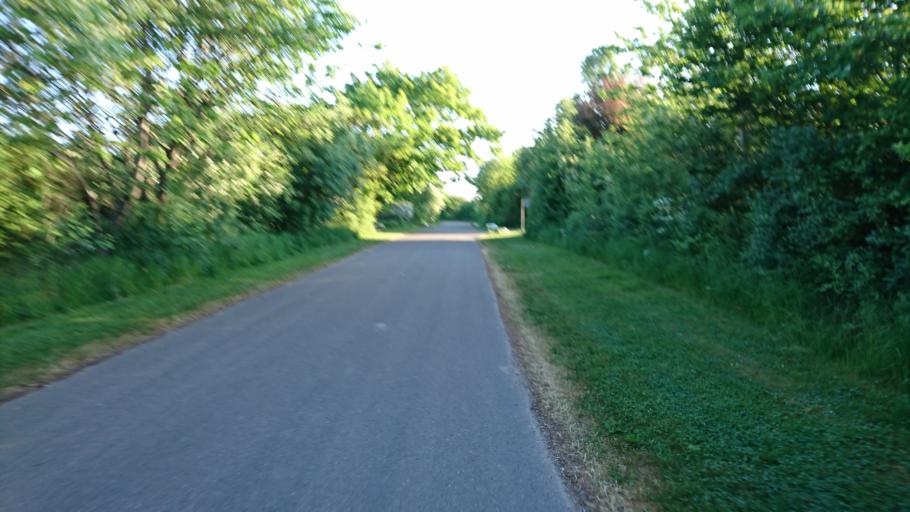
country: DK
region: Capital Region
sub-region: Ballerup Kommune
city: Ballerup
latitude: 55.7147
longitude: 12.3333
